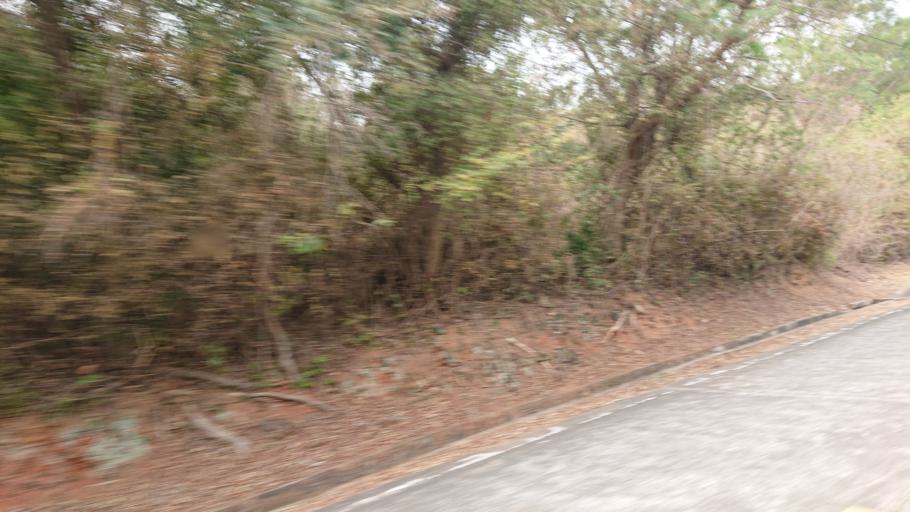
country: TW
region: Fukien
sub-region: Kinmen
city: Jincheng
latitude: 24.4418
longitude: 118.2515
